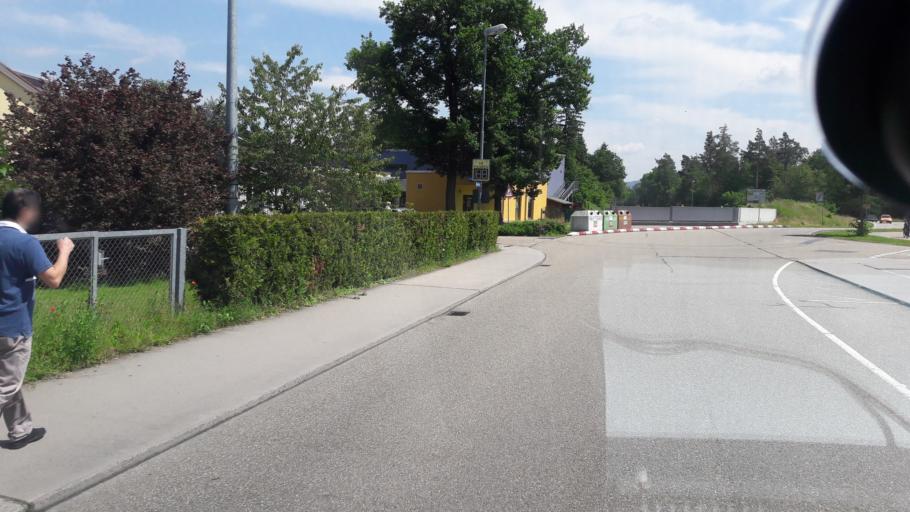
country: DE
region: Baden-Wuerttemberg
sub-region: Karlsruhe Region
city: Rheinstetten
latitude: 48.9622
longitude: 8.3402
